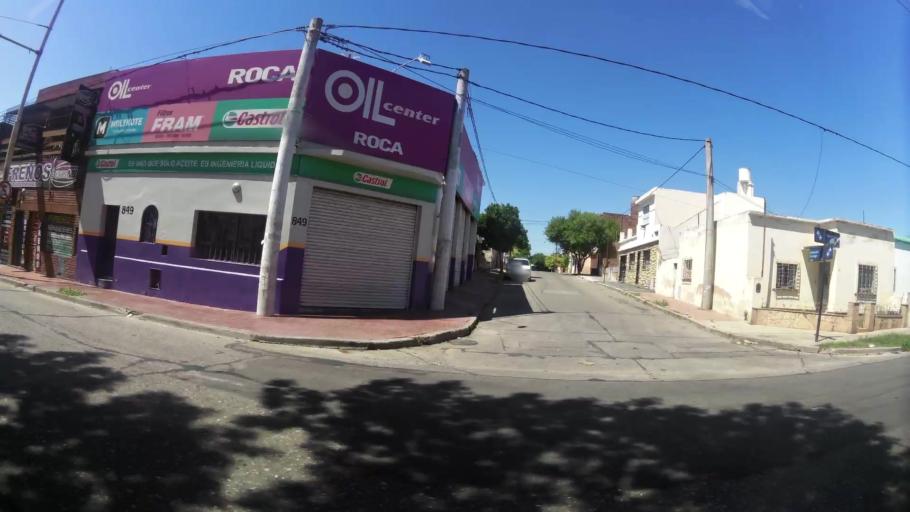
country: AR
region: Cordoba
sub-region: Departamento de Capital
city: Cordoba
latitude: -31.4286
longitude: -64.2040
